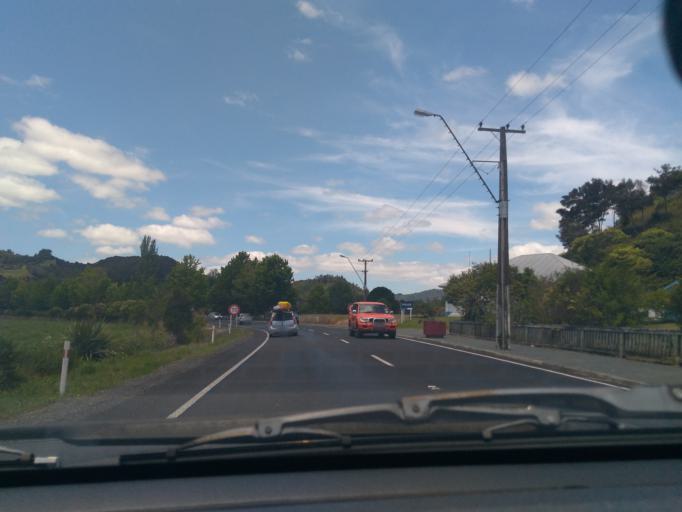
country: NZ
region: Northland
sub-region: Far North District
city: Kerikeri
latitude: -35.1007
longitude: 173.7817
